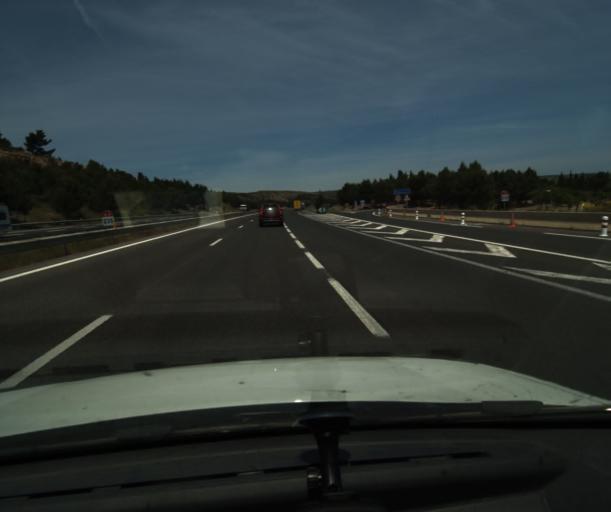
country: FR
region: Languedoc-Roussillon
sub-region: Departement des Pyrenees-Orientales
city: Salses-le-Chateau
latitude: 42.8381
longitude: 2.9105
